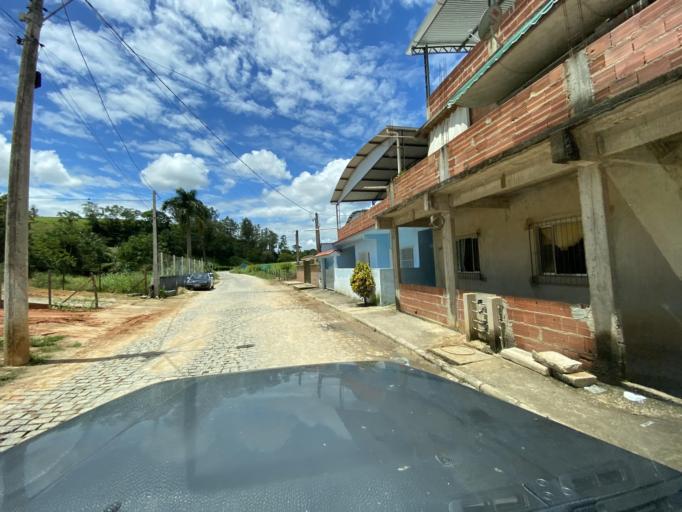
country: BR
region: Espirito Santo
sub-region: Jeronimo Monteiro
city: Jeronimo Monteiro
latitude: -20.7819
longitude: -41.3889
